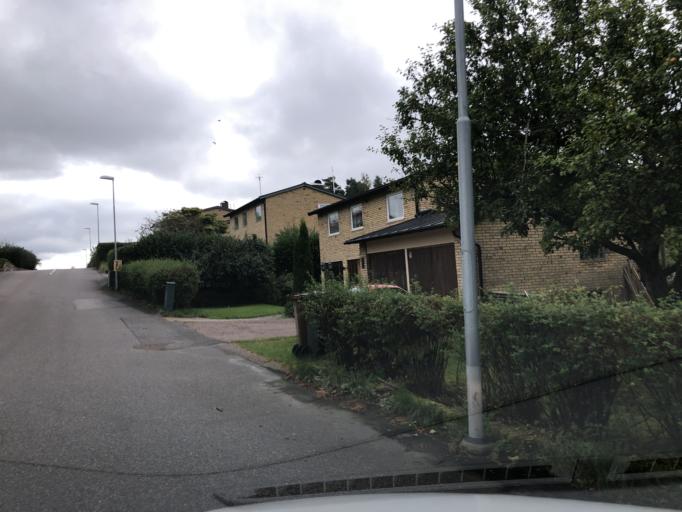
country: SE
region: Vaestra Goetaland
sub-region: Goteborg
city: Majorna
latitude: 57.7409
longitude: 11.9079
